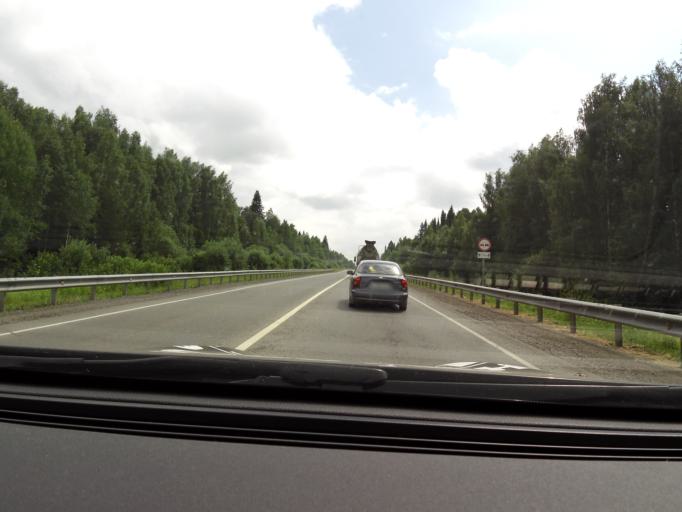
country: RU
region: Perm
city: Kungur
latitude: 57.3254
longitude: 56.9599
